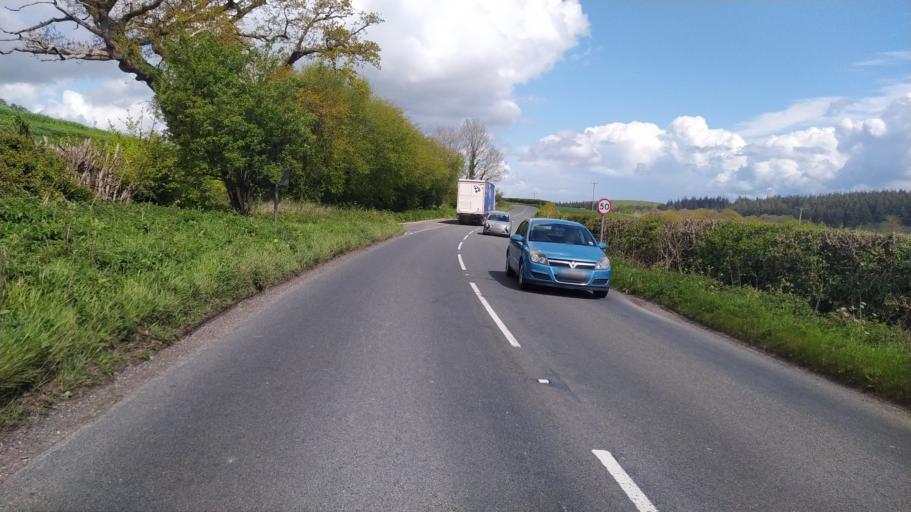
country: GB
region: England
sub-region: Wiltshire
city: Kilmington
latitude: 51.1607
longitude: -2.2930
